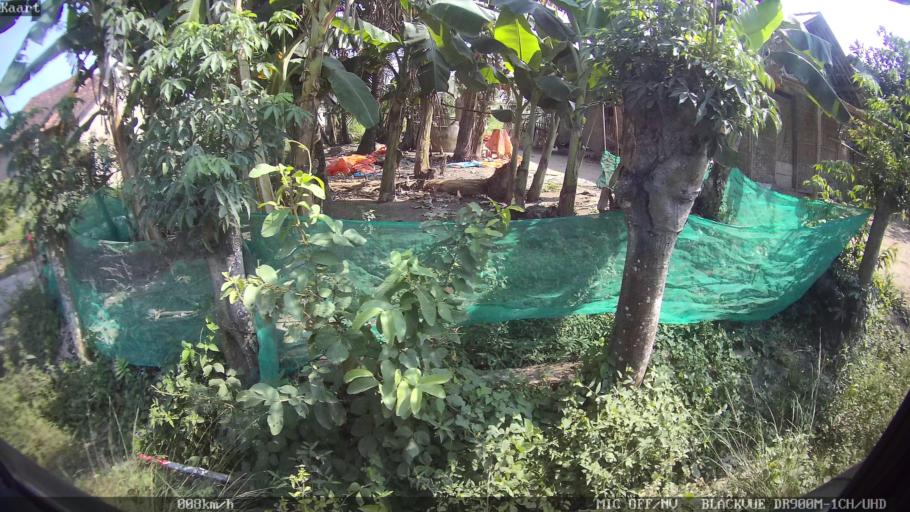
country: ID
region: Lampung
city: Natar
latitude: -5.2641
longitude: 105.2124
